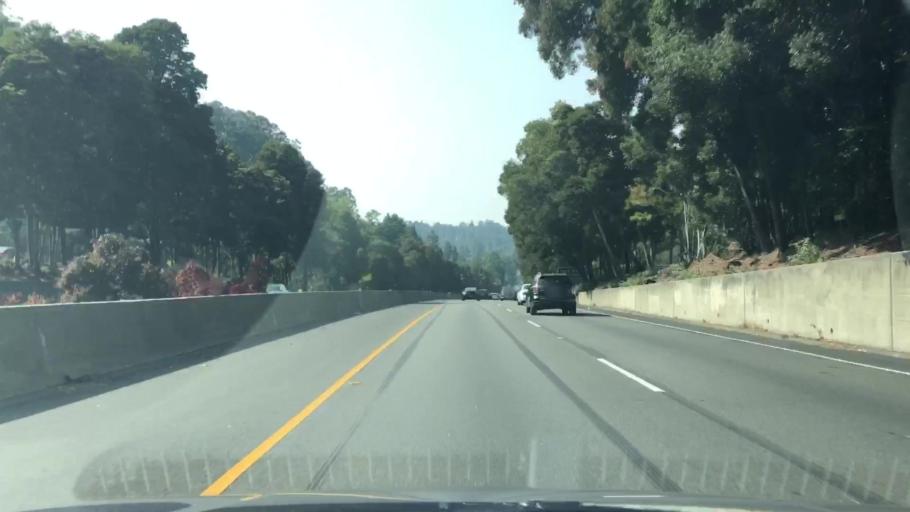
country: US
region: California
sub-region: Alameda County
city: Piedmont
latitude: 37.8126
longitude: -122.1998
